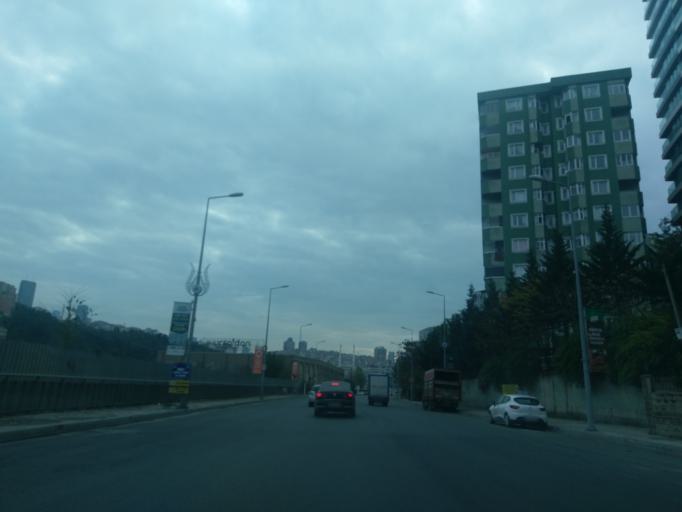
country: TR
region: Istanbul
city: Sisli
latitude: 41.0944
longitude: 28.9805
